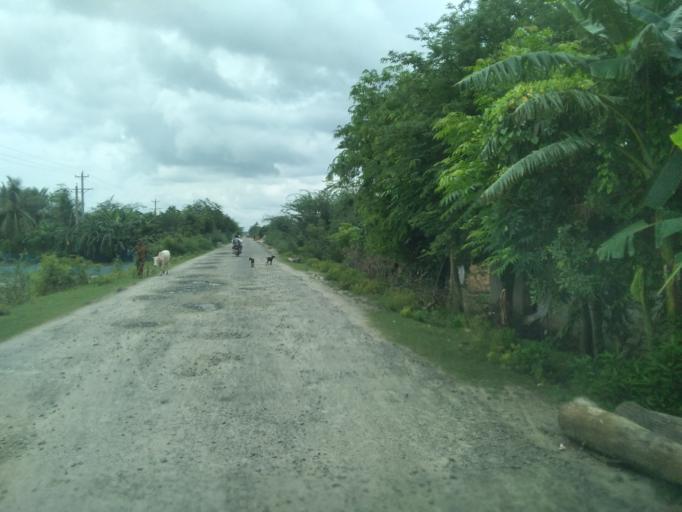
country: IN
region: West Bengal
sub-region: North 24 Parganas
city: Gosaba
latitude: 22.2665
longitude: 89.1736
